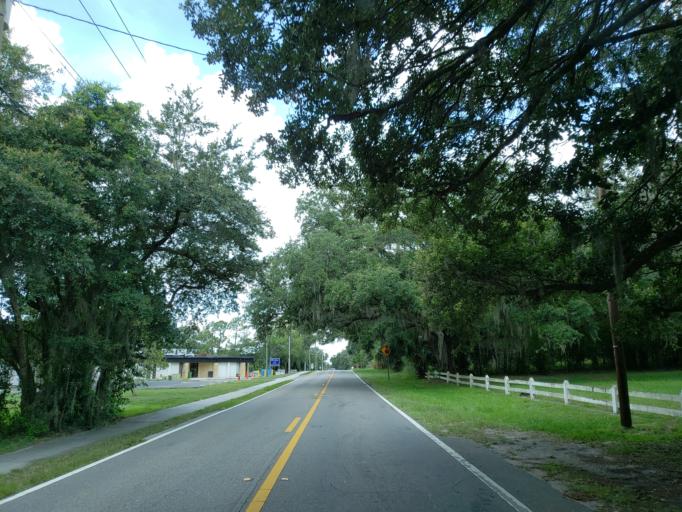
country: US
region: Florida
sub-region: Hillsborough County
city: Mango
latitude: 27.9961
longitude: -82.3005
